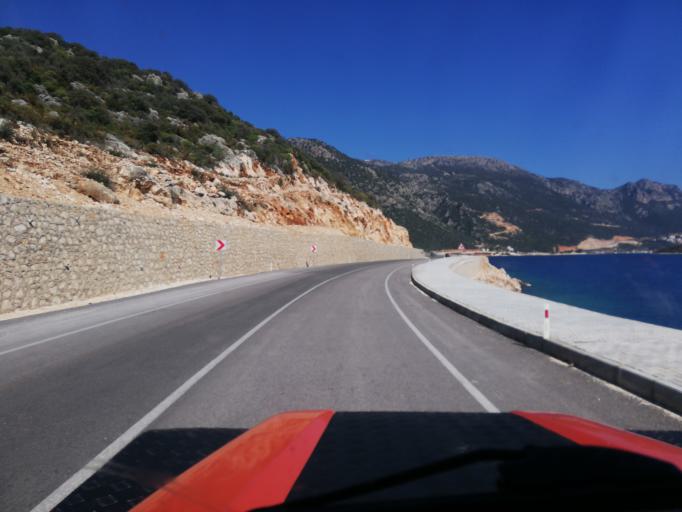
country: TR
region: Antalya
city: Kas
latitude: 36.2036
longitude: 29.5971
